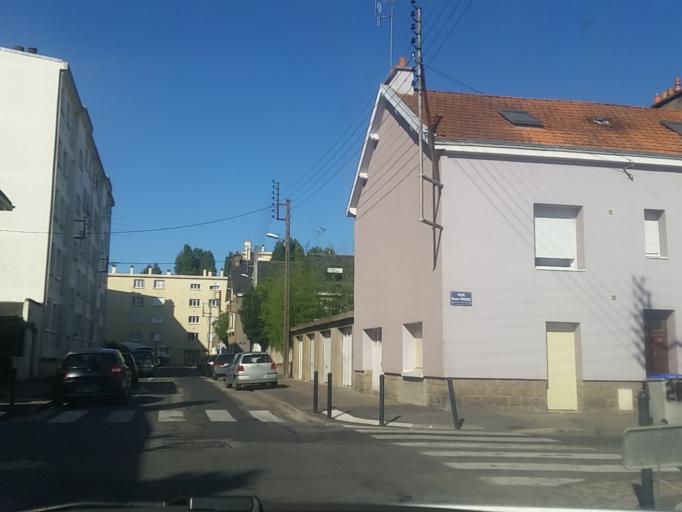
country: FR
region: Pays de la Loire
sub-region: Departement de la Loire-Atlantique
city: Nantes
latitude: 47.2003
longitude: -1.5464
